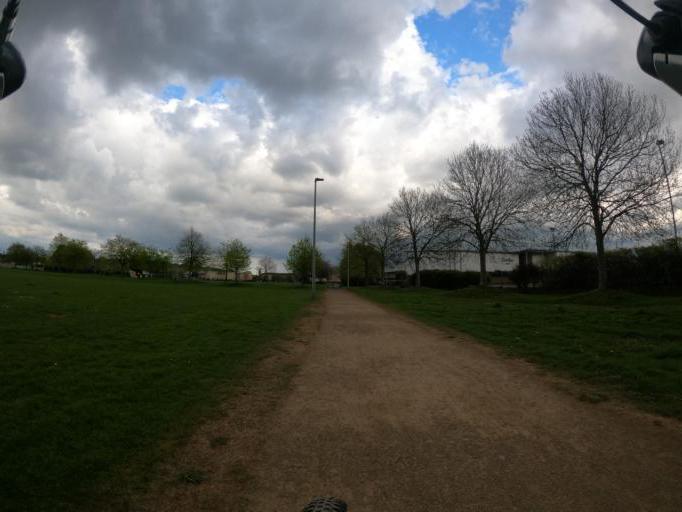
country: GB
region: Scotland
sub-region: Edinburgh
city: Currie
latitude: 55.9397
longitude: -3.3048
